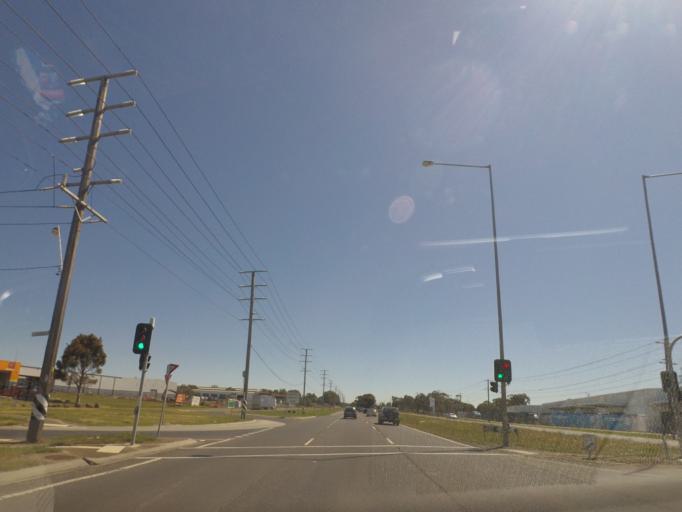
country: AU
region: Victoria
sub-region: Hume
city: Roxburgh Park
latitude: -37.6284
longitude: 144.9487
